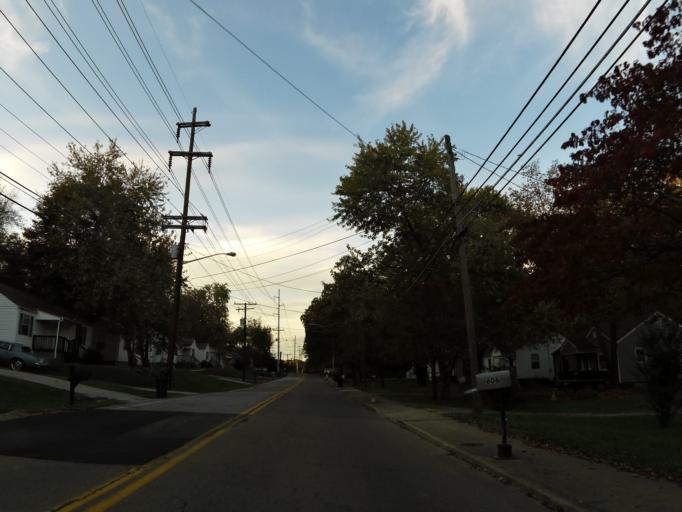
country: US
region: Tennessee
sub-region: Knox County
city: Knoxville
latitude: 35.9465
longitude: -83.9809
